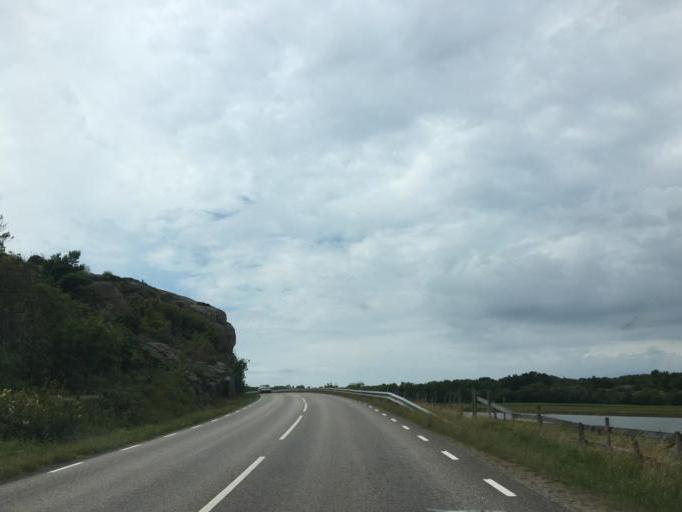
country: SE
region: Vaestra Goetaland
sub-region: Sotenas Kommun
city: Hunnebostrand
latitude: 58.4246
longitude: 11.2933
